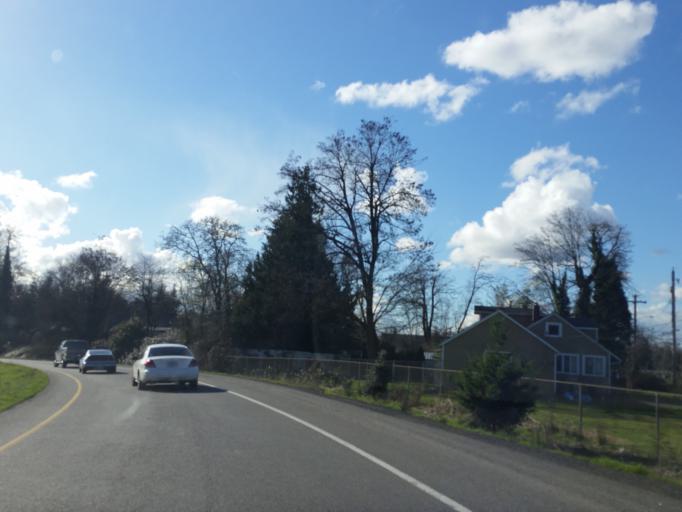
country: US
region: Washington
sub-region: Pierce County
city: Sumner
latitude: 47.1934
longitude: -122.2301
